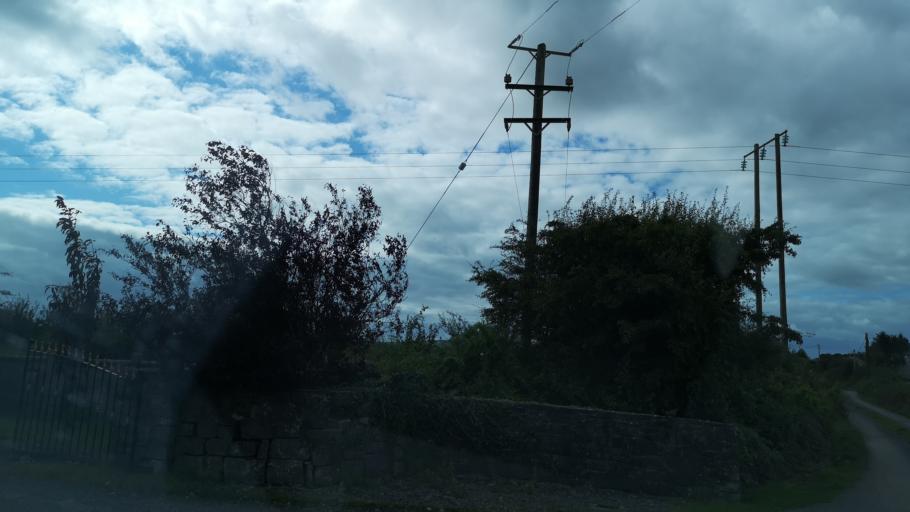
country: IE
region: Connaught
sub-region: County Galway
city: Moycullen
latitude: 53.3186
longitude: -9.1383
